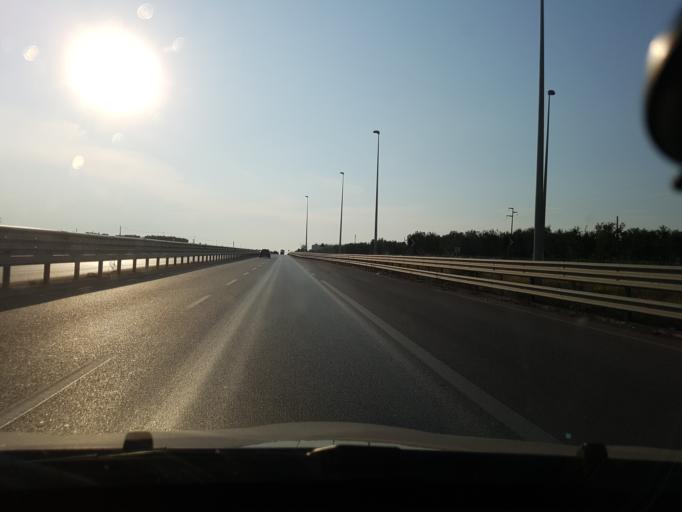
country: IT
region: Apulia
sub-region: Provincia di Foggia
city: Cerignola
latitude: 41.2793
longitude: 15.8587
